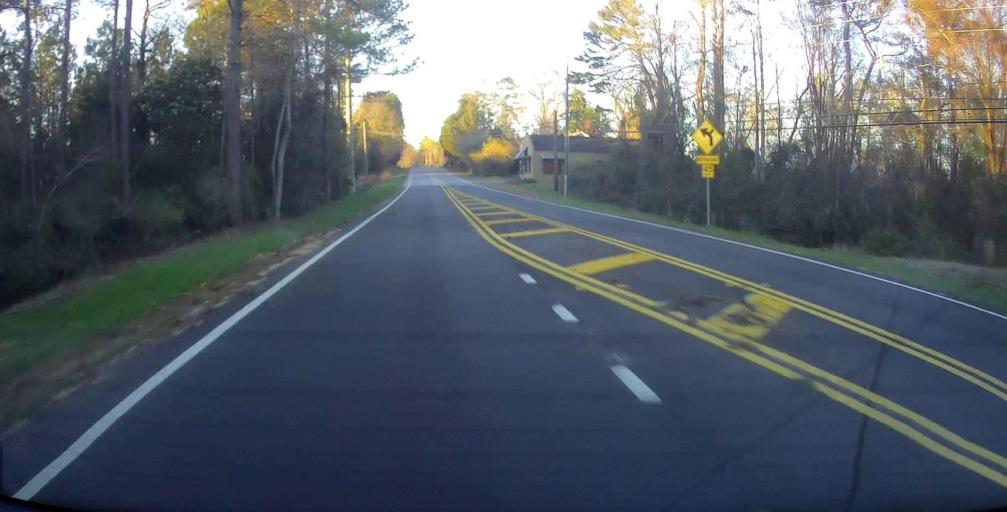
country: US
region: Alabama
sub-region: Russell County
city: Phenix City
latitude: 32.5462
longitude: -84.9954
